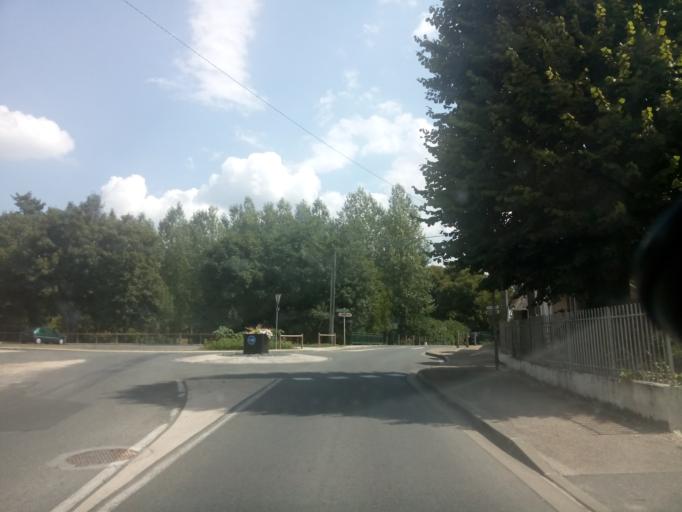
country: FR
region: Centre
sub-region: Departement d'Indre-et-Loire
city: Azay-le-Rideau
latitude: 47.2650
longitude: 0.4468
